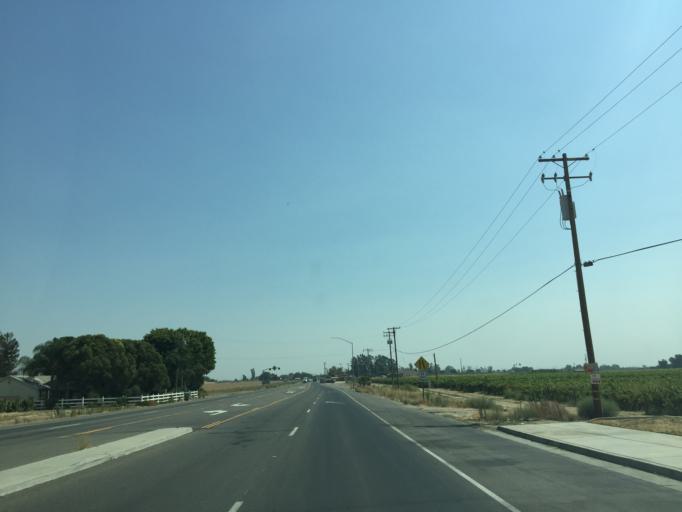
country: US
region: California
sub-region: Fresno County
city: Selma
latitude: 36.5610
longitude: -119.6289
